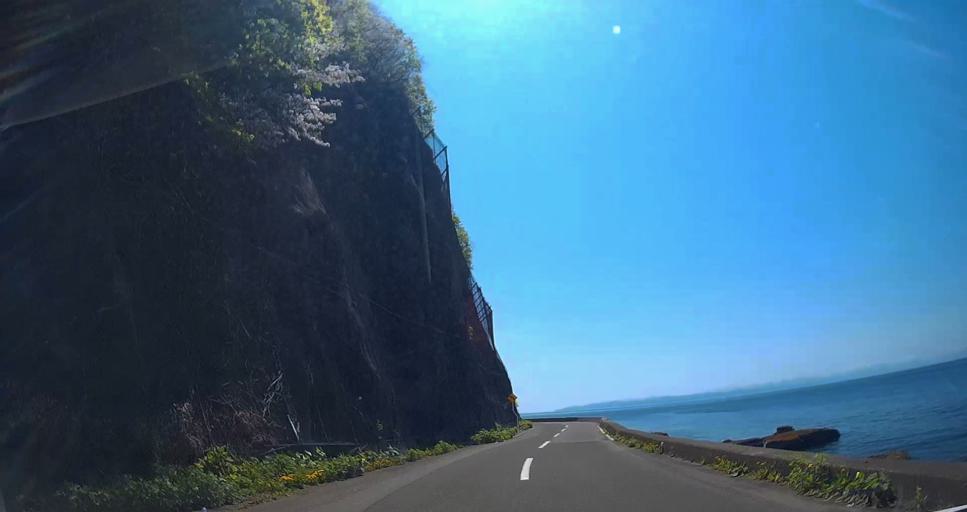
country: JP
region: Aomori
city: Aomori Shi
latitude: 41.1336
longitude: 140.7802
